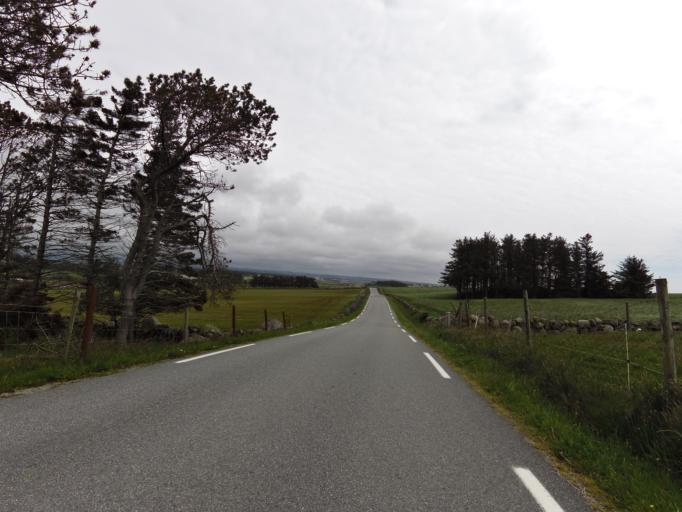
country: NO
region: Rogaland
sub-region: Ha
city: Naerbo
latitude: 58.6589
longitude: 5.5627
